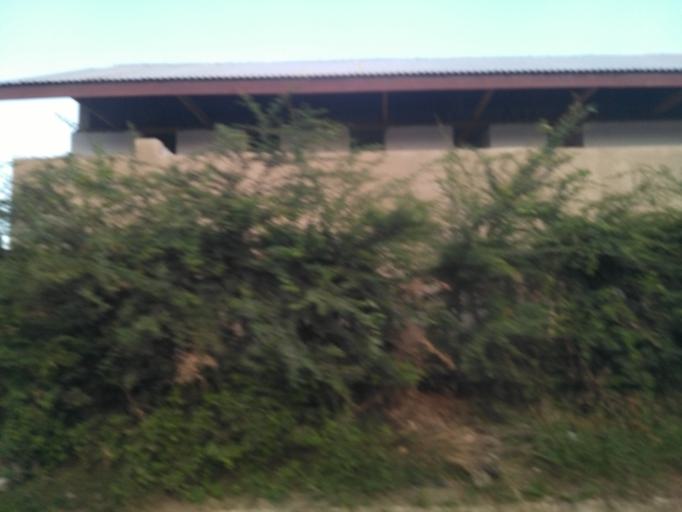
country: TZ
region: Dar es Salaam
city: Magomeni
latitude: -6.7798
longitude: 39.2652
